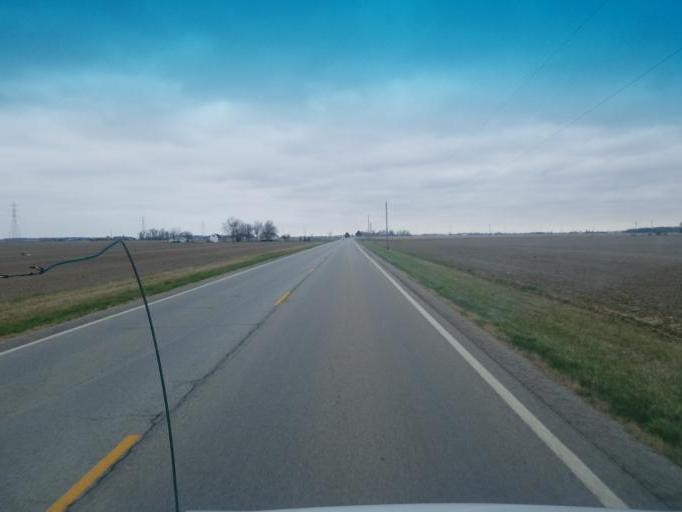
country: US
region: Ohio
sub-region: Allen County
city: Delphos
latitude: 40.9320
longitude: -84.4471
